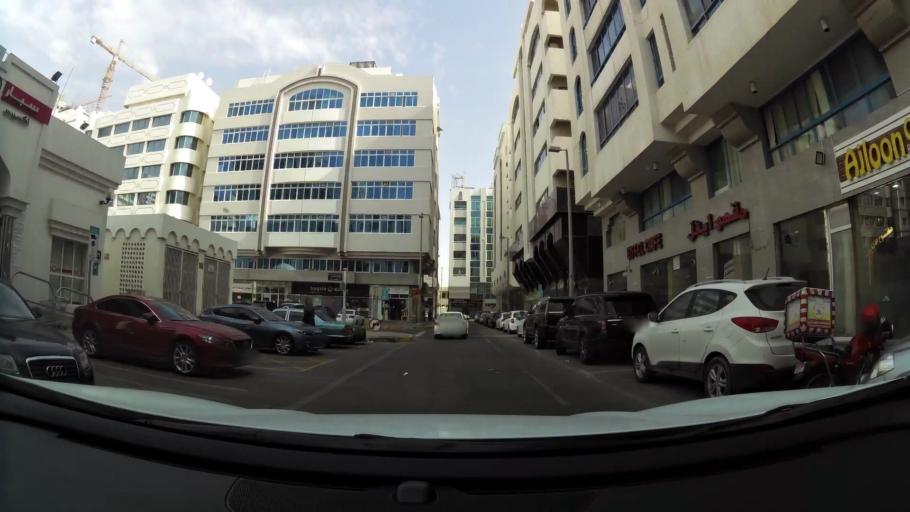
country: AE
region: Abu Dhabi
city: Abu Dhabi
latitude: 24.4712
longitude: 54.3481
